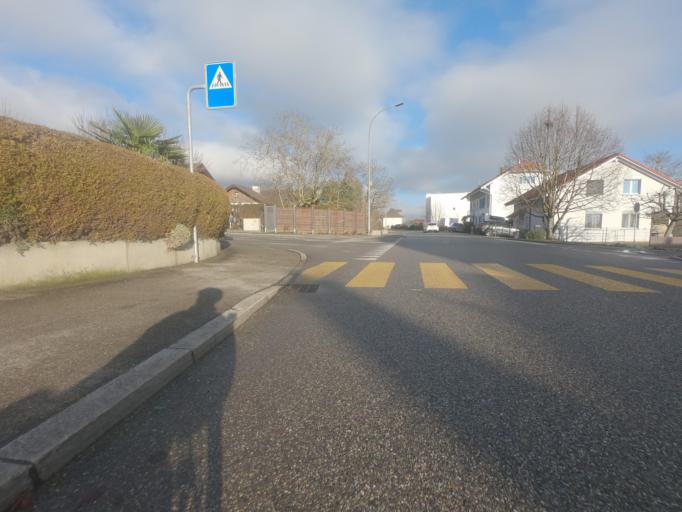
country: CH
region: Solothurn
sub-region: Bezirk Lebern
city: Bettlach
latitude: 47.1993
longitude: 7.4172
